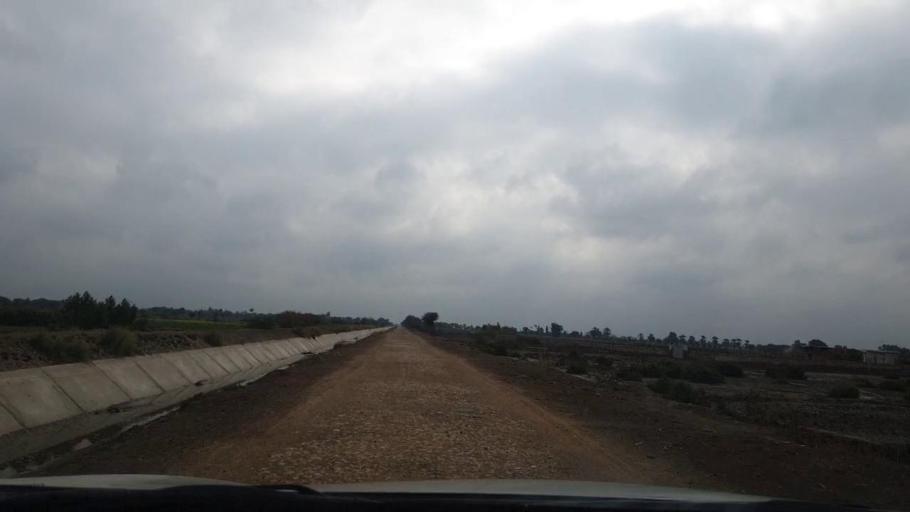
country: PK
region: Sindh
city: Tando Mittha Khan
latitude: 25.8836
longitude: 69.1348
